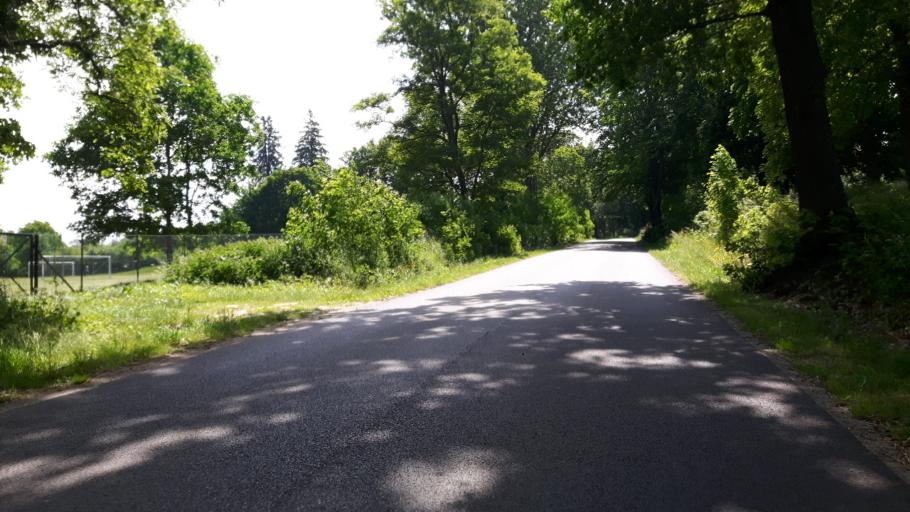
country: PL
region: Pomeranian Voivodeship
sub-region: Powiat wejherowski
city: Choczewo
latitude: 54.7489
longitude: 17.7949
